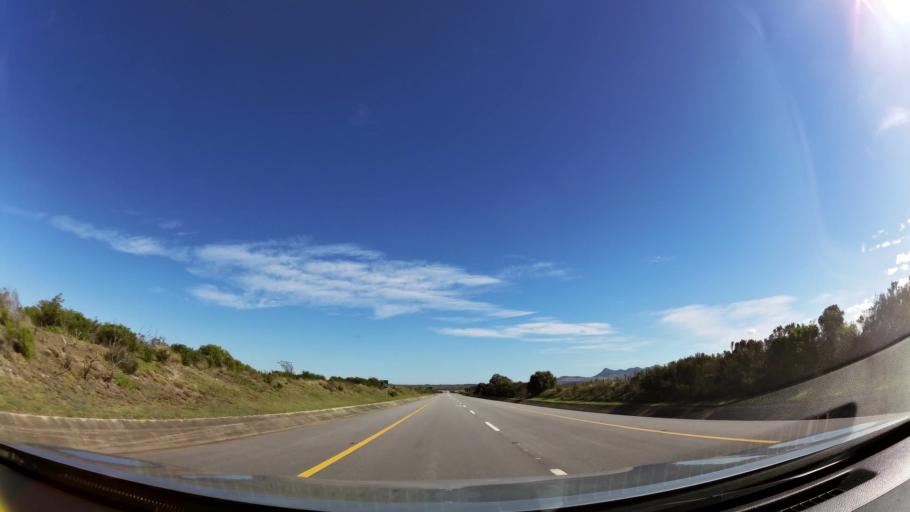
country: ZA
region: Eastern Cape
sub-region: Cacadu District Municipality
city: Kruisfontein
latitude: -34.0249
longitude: 24.6087
